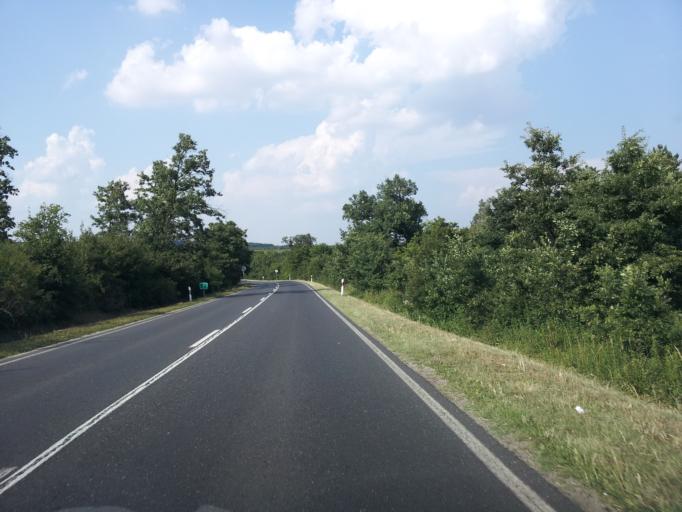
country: HU
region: Veszprem
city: Nemesvamos
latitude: 47.0331
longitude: 17.9136
